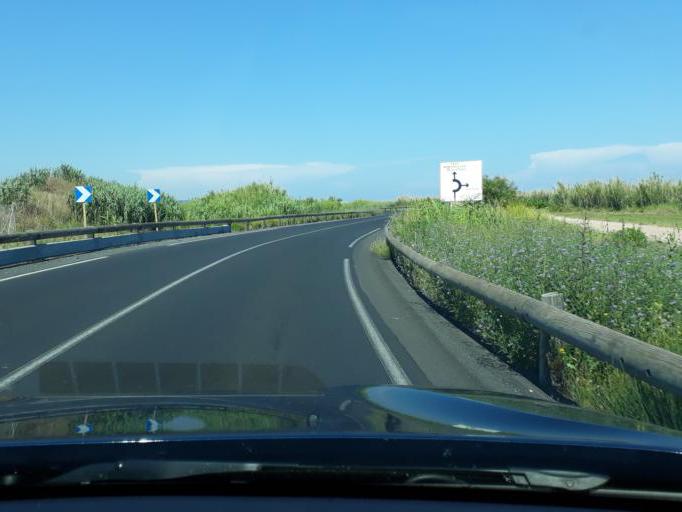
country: FR
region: Languedoc-Roussillon
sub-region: Departement de l'Herault
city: Marseillan
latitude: 43.3543
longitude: 3.5943
